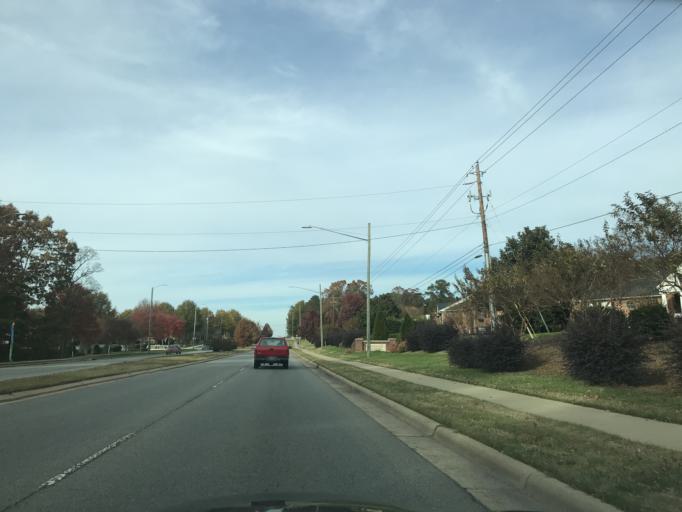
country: US
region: North Carolina
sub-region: Wake County
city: West Raleigh
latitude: 35.8945
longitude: -78.6803
